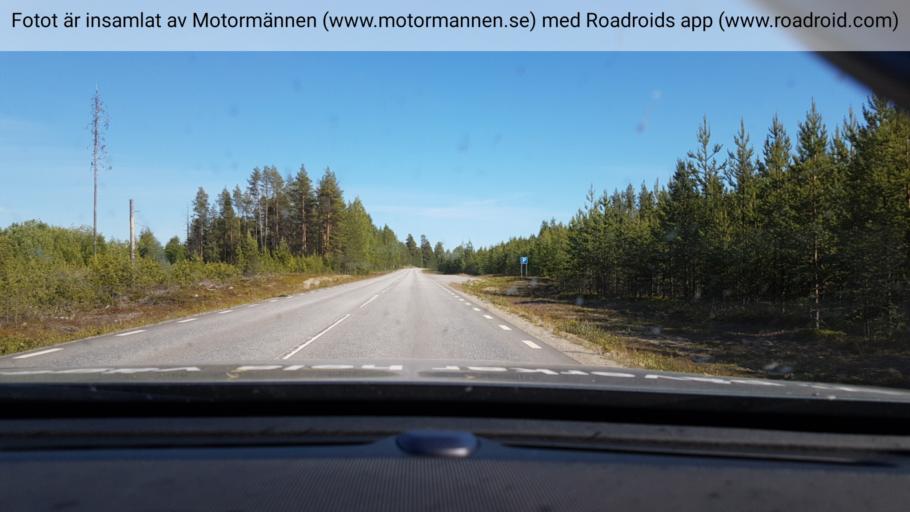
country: SE
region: Vaesterbotten
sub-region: Lycksele Kommun
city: Lycksele
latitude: 64.6263
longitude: 18.6290
